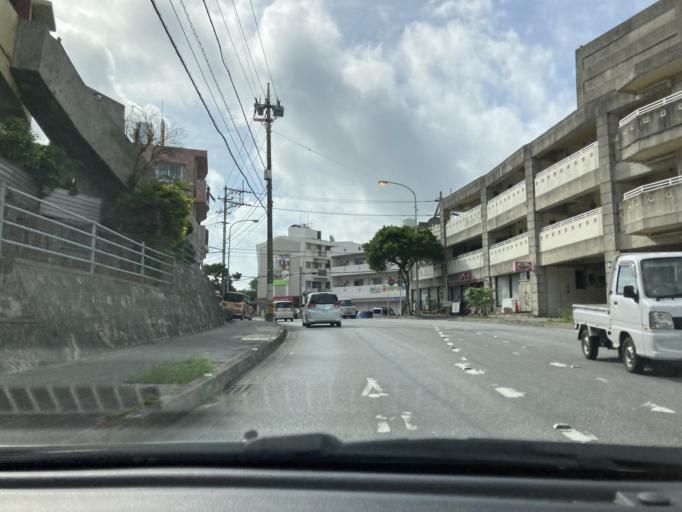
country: JP
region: Okinawa
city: Ginowan
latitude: 26.2604
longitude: 127.7638
